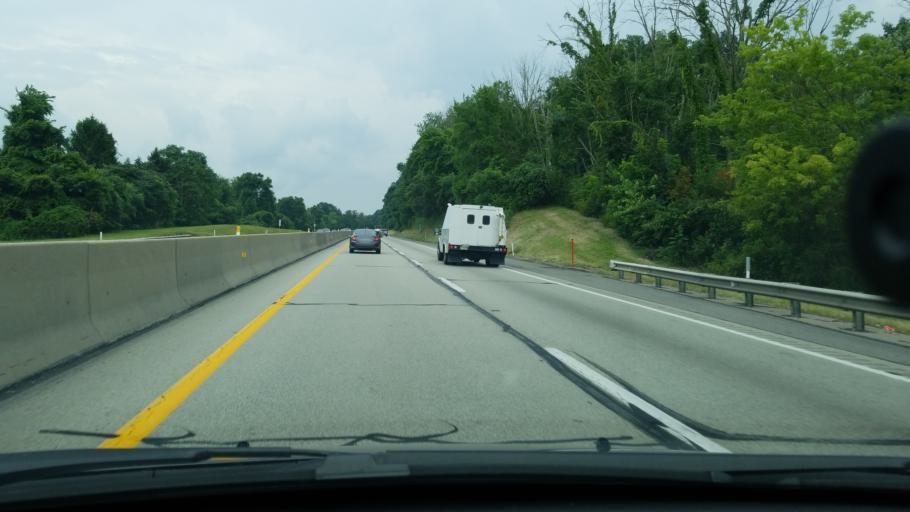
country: US
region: Pennsylvania
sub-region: Allegheny County
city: Plum
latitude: 40.4861
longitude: -79.7773
